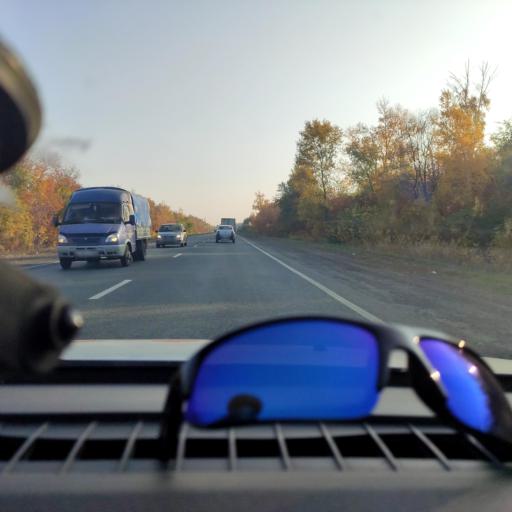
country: RU
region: Samara
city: Novokuybyshevsk
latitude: 52.9933
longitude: 49.9451
